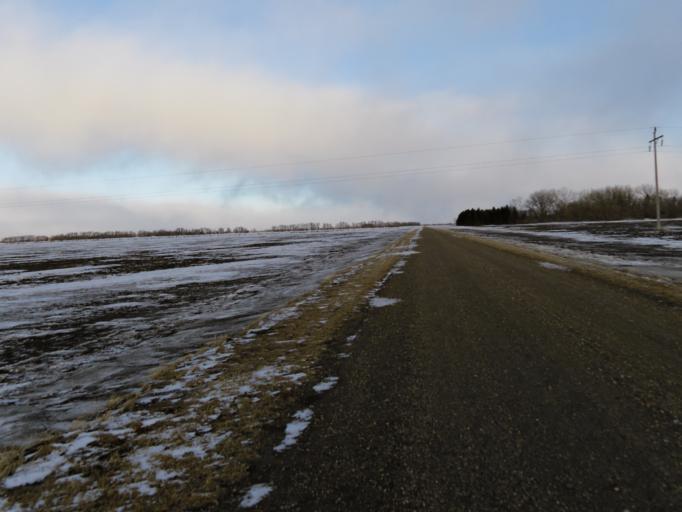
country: US
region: North Dakota
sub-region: Walsh County
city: Grafton
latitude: 48.3976
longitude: -97.2329
